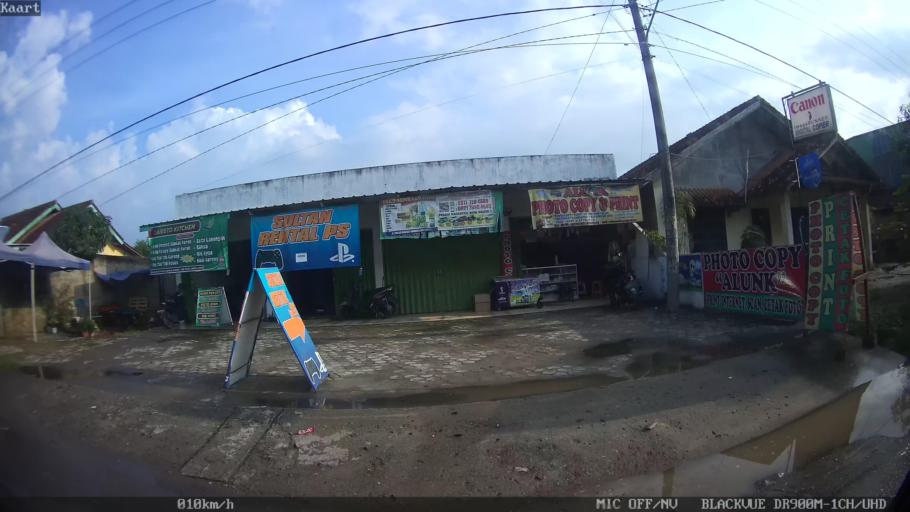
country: ID
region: Lampung
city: Kedaton
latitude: -5.3943
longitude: 105.3141
